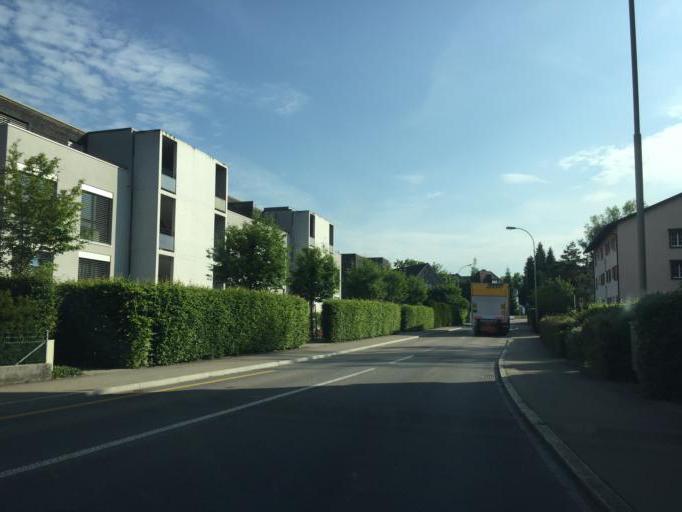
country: CH
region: Zurich
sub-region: Bezirk Dielsdorf
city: Oberglatt
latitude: 47.4748
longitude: 8.5160
